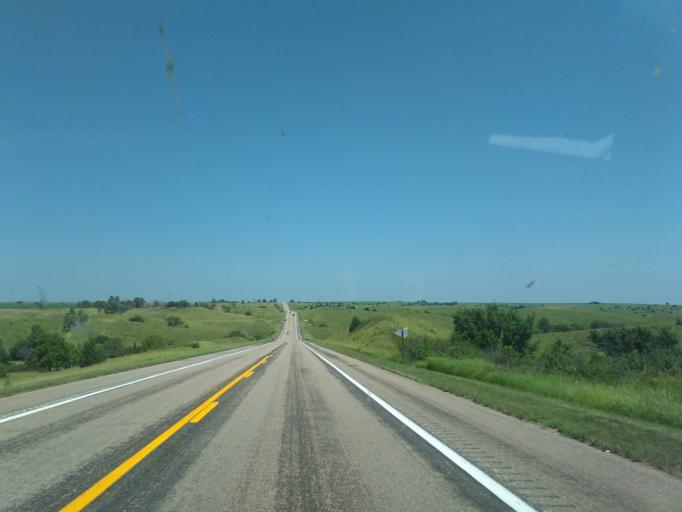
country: US
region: Nebraska
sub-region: Frontier County
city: Stockville
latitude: 40.5818
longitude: -100.6296
